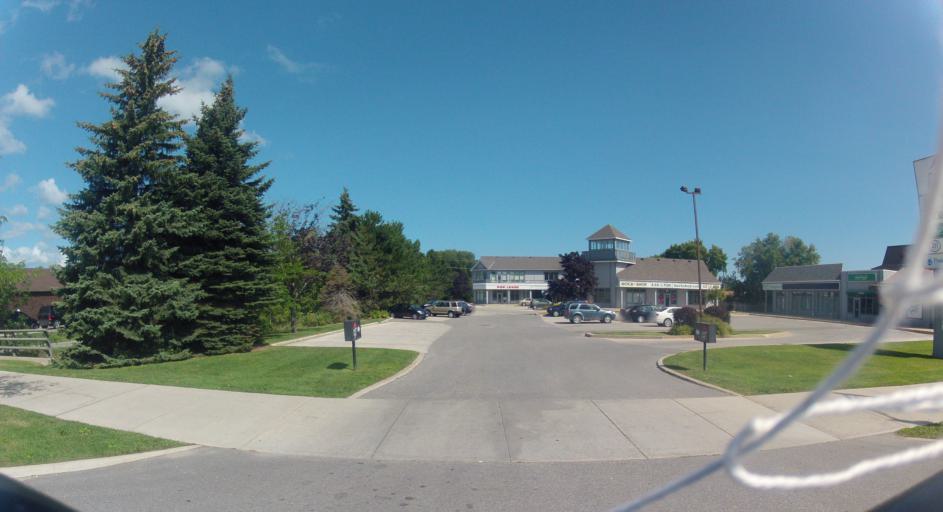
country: CA
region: Ontario
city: Collingwood
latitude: 44.5022
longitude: -80.2249
